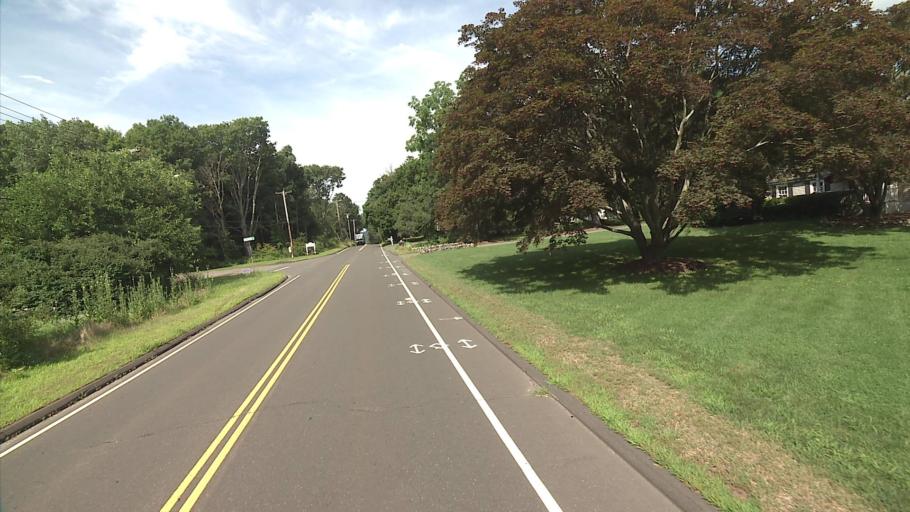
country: US
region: Connecticut
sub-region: New Haven County
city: Woodbridge
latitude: 41.3289
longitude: -73.0166
